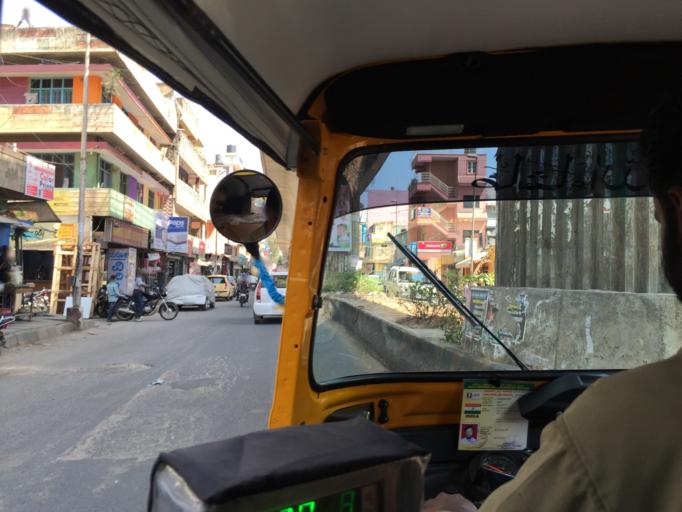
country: IN
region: Karnataka
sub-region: Bangalore Urban
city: Bangalore
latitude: 12.9785
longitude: 77.6295
